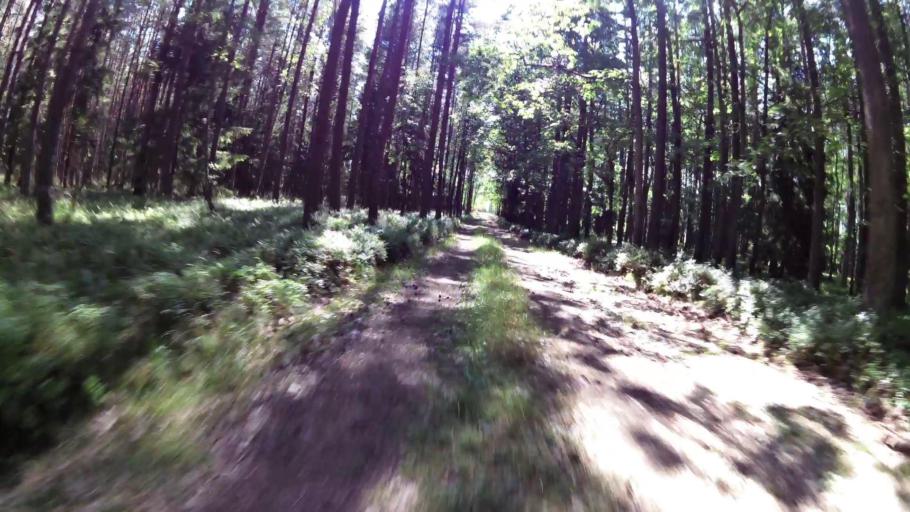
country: PL
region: West Pomeranian Voivodeship
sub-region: Powiat drawski
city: Czaplinek
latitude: 53.4458
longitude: 16.2287
